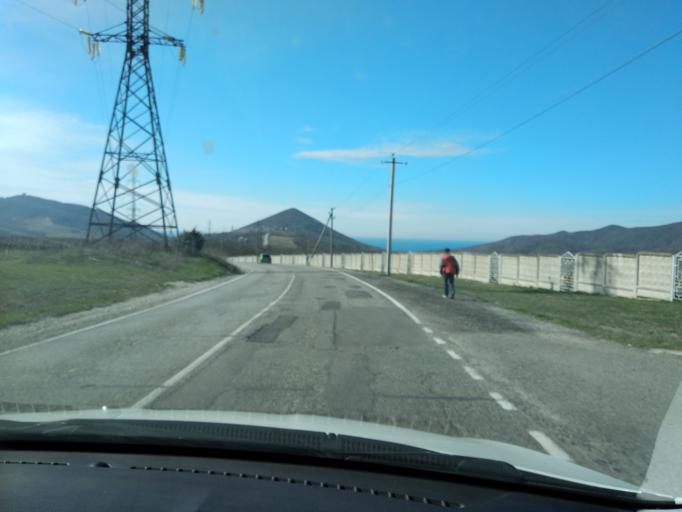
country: RU
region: Krasnodarskiy
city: Myskhako
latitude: 44.7054
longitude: 37.7180
